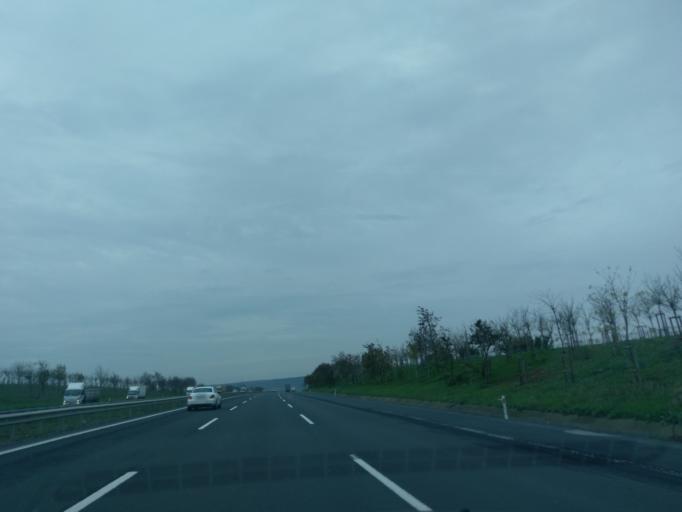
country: TR
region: Istanbul
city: Canta
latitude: 41.1418
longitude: 28.1491
